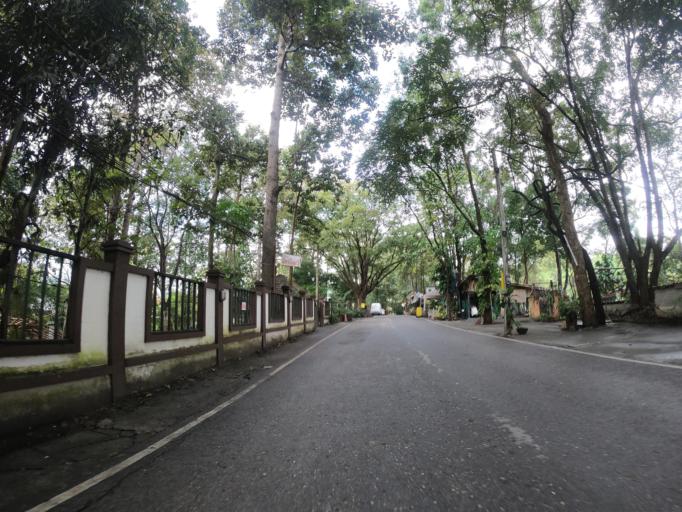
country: TH
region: Chiang Mai
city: Chiang Mai
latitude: 18.8200
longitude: 98.9743
